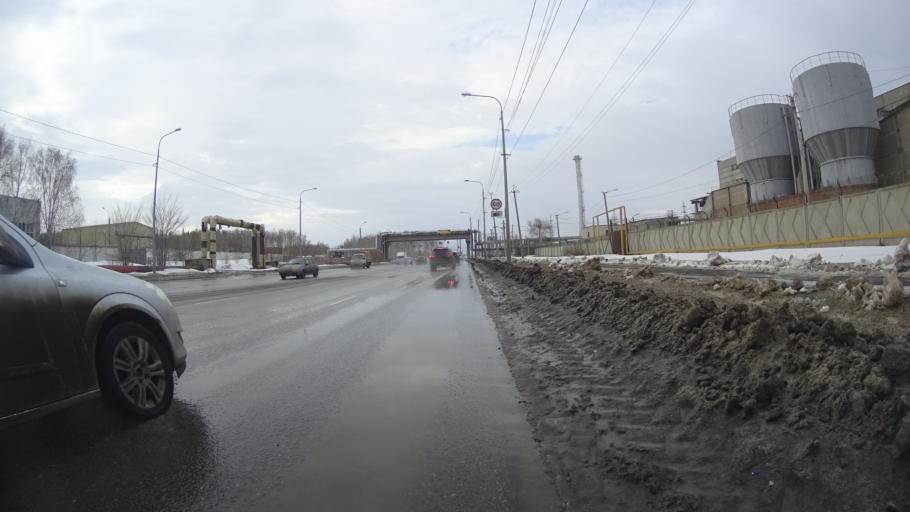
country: RU
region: Chelyabinsk
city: Roshchino
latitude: 55.2069
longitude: 61.3197
